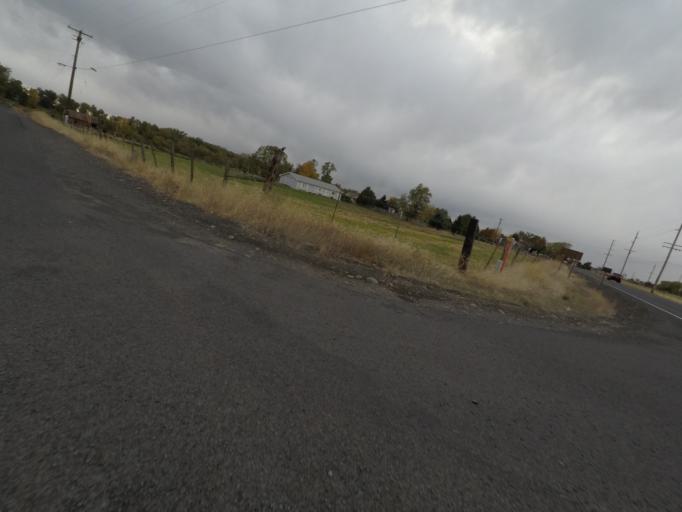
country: US
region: Washington
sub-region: Walla Walla County
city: Walla Walla East
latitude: 46.0863
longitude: -118.2525
